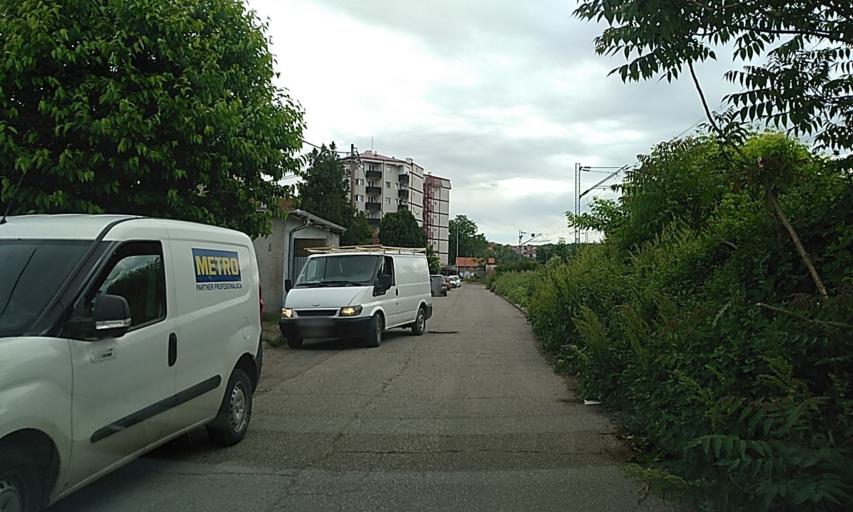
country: RS
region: Central Serbia
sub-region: Nisavski Okrug
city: Nis
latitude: 43.3204
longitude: 21.8869
